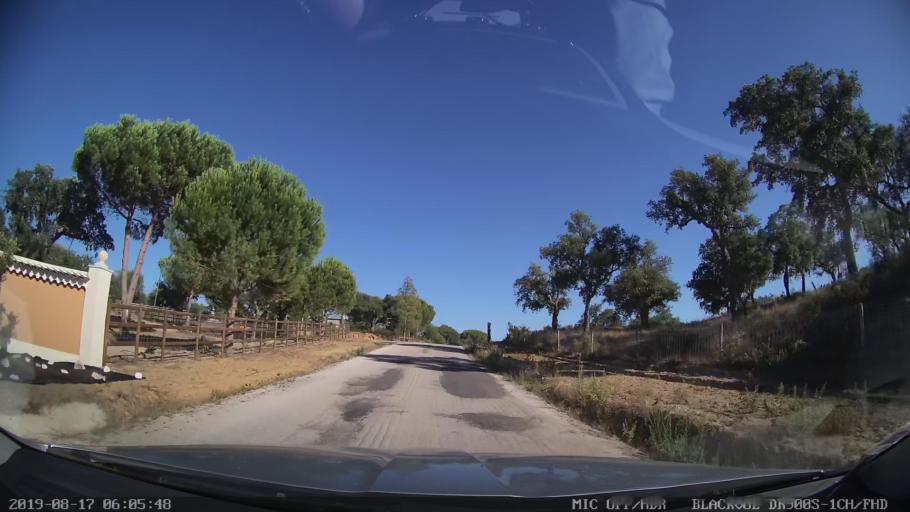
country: PT
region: Santarem
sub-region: Benavente
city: Poceirao
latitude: 38.8474
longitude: -8.6944
